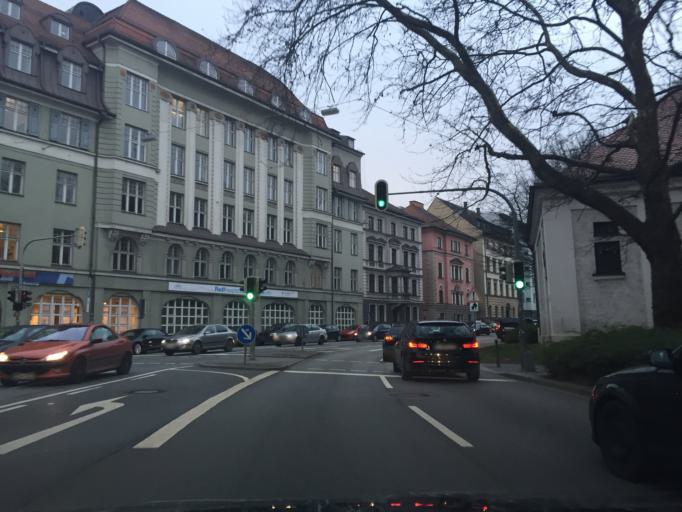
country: DE
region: Bavaria
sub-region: Upper Bavaria
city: Munich
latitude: 48.1319
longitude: 11.5707
